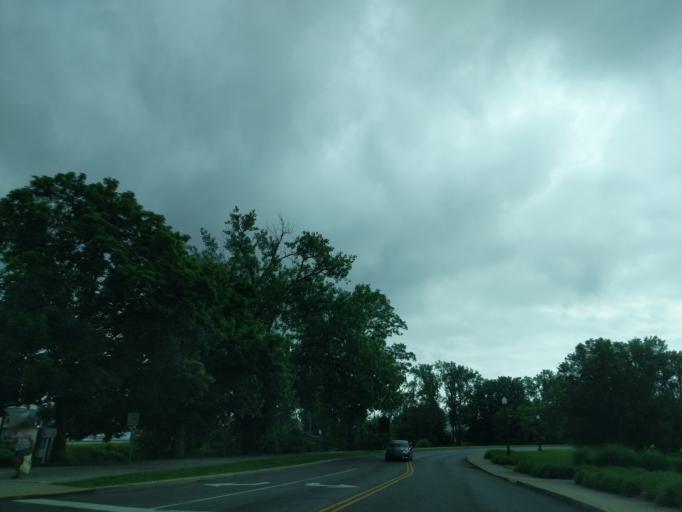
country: US
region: Indiana
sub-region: Delaware County
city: Muncie
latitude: 40.1973
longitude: -85.3897
